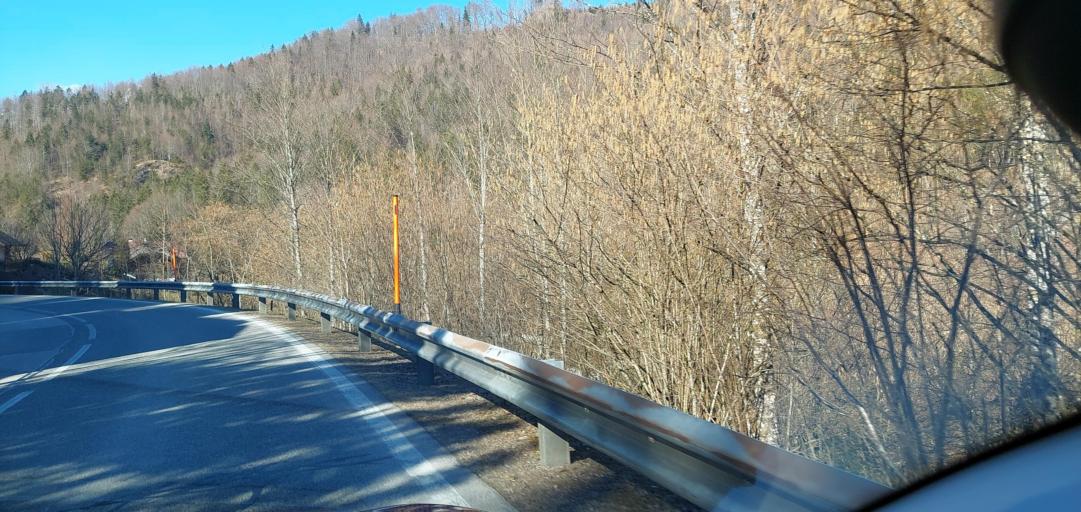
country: AT
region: Upper Austria
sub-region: Politischer Bezirk Gmunden
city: Bad Ischl
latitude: 47.7446
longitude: 13.6647
